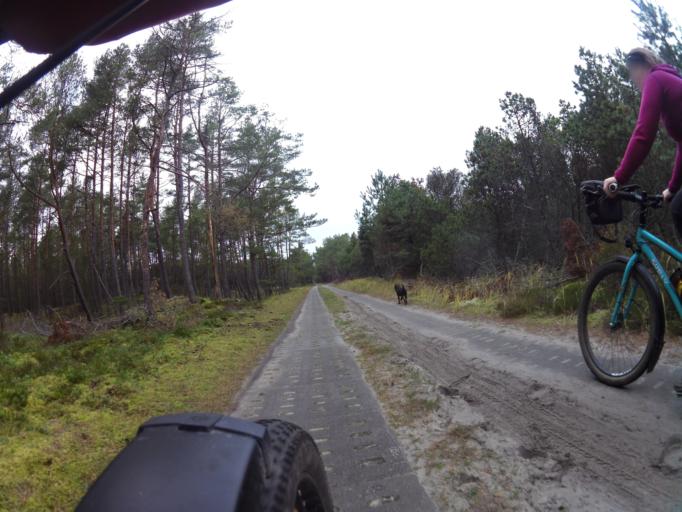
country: PL
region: Pomeranian Voivodeship
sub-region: Powiat pucki
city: Hel
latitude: 54.6278
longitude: 18.8136
